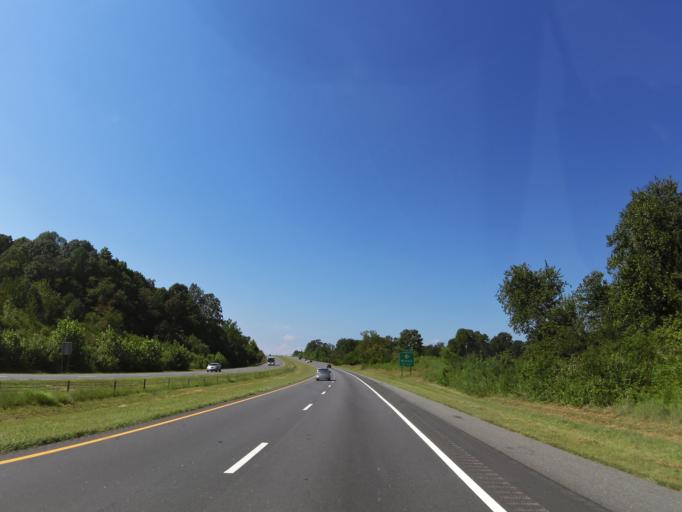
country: US
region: North Carolina
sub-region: Catawba County
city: Newton
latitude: 35.6266
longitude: -81.2907
